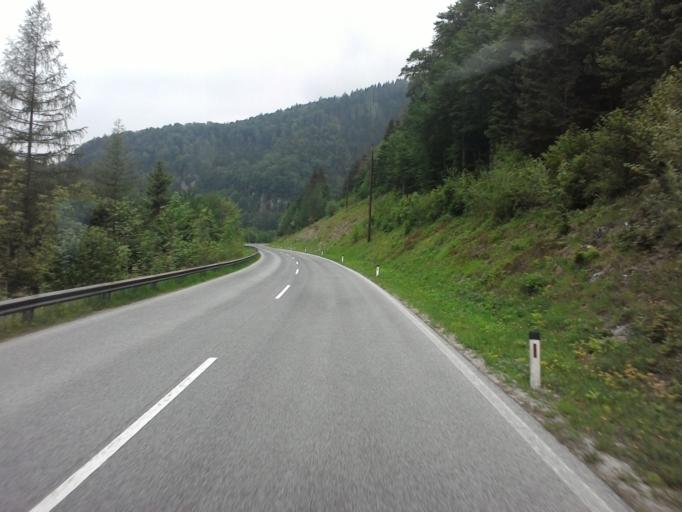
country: AT
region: Styria
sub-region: Politischer Bezirk Liezen
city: Palfau
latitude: 47.7112
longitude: 14.8378
